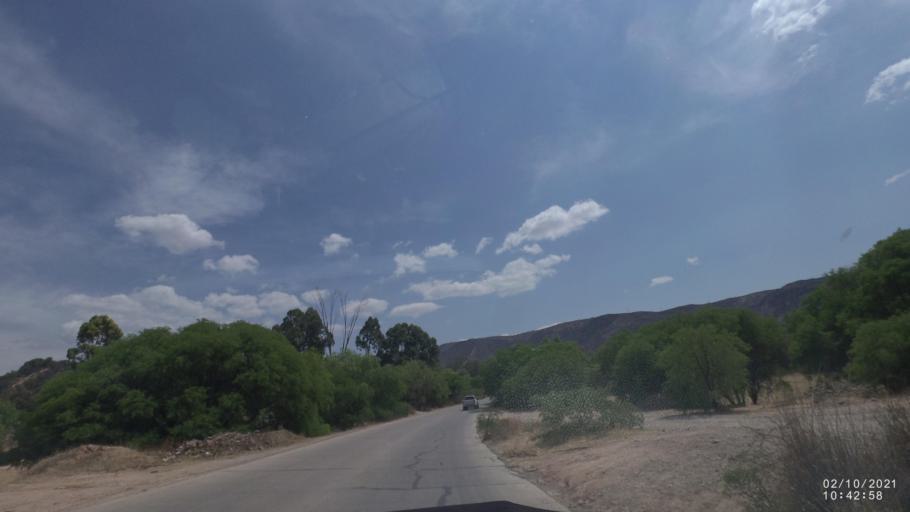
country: BO
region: Cochabamba
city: Capinota
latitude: -17.6022
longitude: -66.2976
